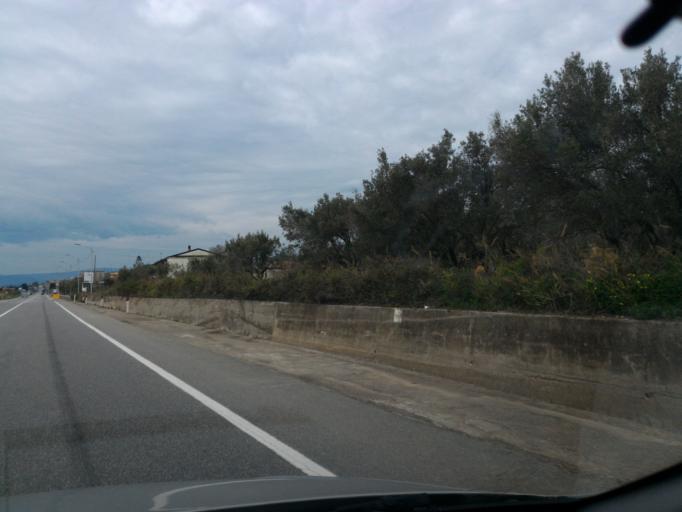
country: IT
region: Calabria
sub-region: Provincia di Catanzaro
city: Barone
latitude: 38.8484
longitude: 16.6611
